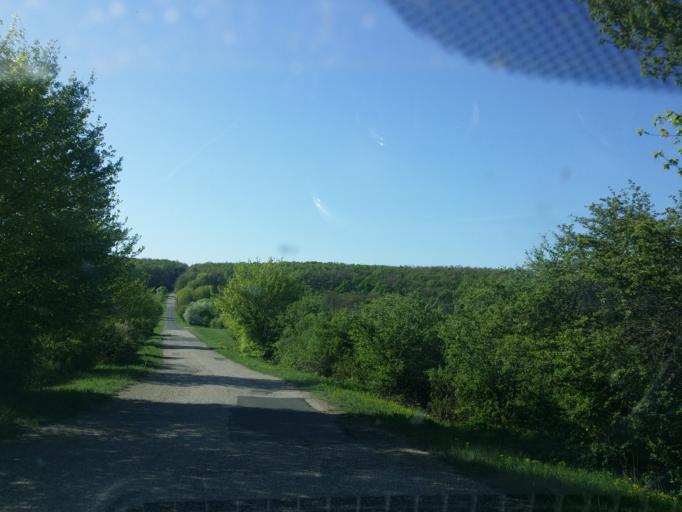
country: HU
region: Pest
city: Nagymaros
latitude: 47.8409
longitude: 18.9514
